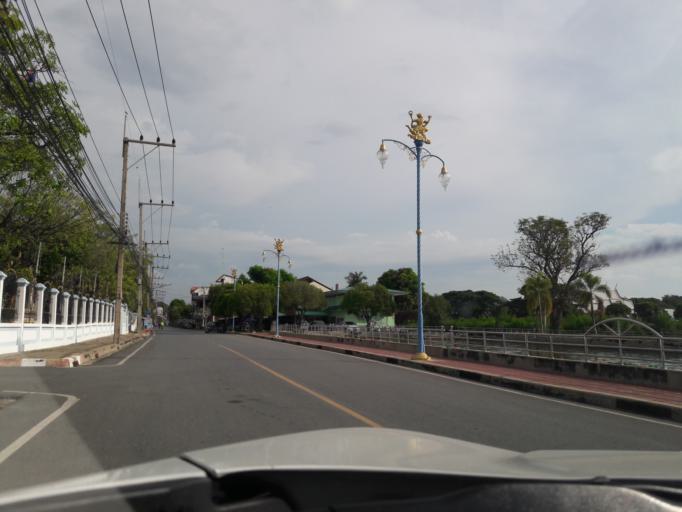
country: TH
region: Lop Buri
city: Ban Mi
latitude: 15.0445
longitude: 100.5367
